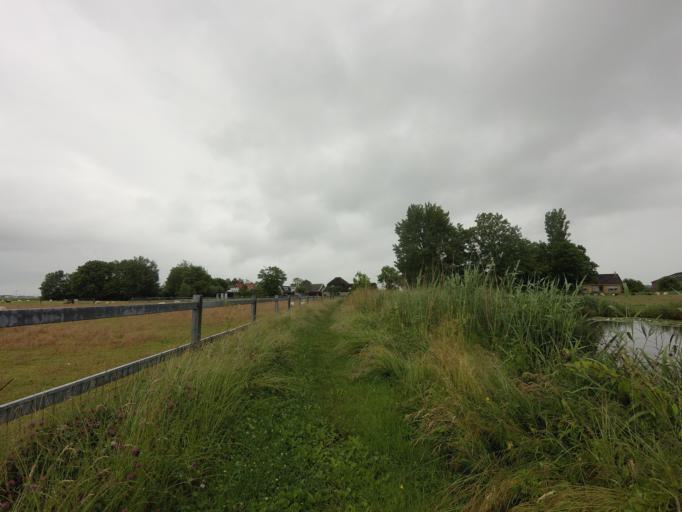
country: NL
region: North Holland
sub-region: Gemeente Schagen
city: Schagen
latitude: 52.7651
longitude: 4.8015
